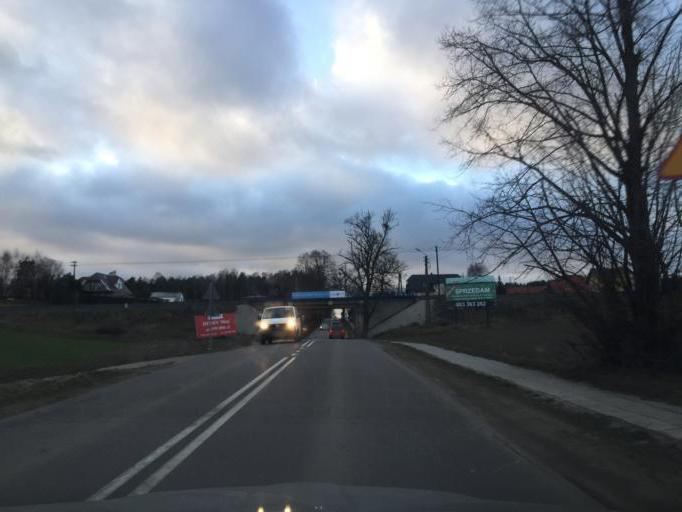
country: PL
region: Pomeranian Voivodeship
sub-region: Powiat kartuski
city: Banino
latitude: 54.3874
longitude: 18.4215
